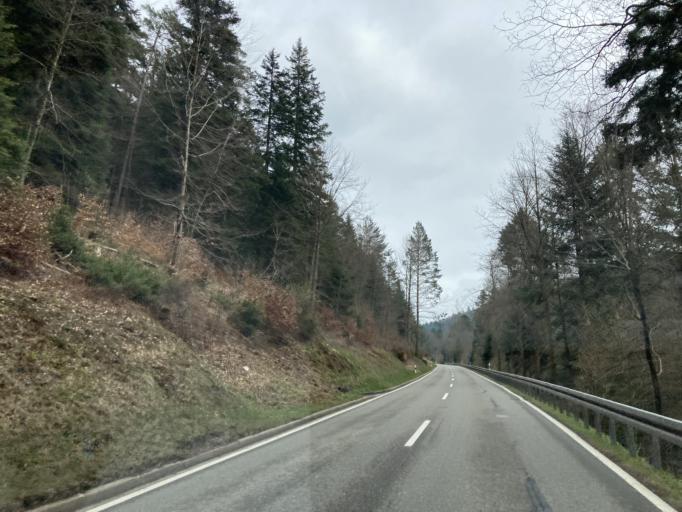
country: DE
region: Baden-Wuerttemberg
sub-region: Karlsruhe Region
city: Hofen an der Enz
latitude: 48.7990
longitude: 8.6061
